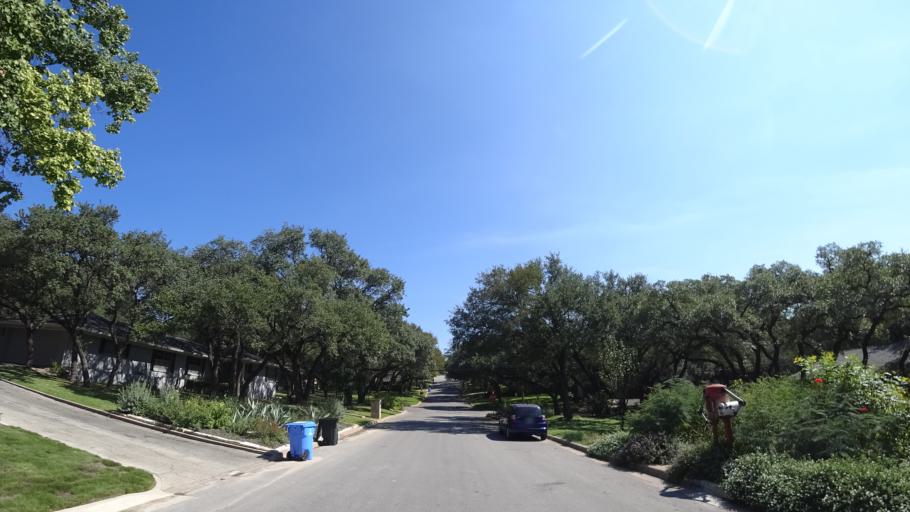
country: US
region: Texas
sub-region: Travis County
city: Rollingwood
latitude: 30.2732
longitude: -97.7895
